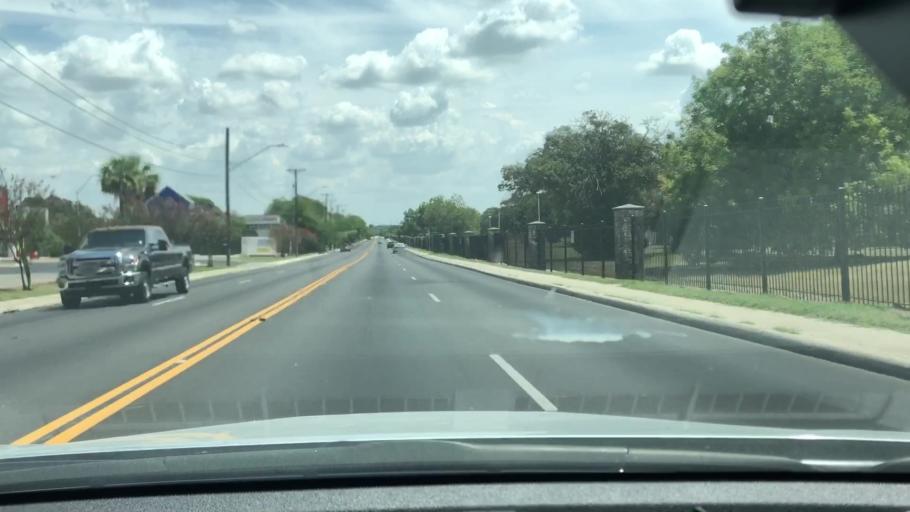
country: US
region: Texas
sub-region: Bexar County
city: Terrell Hills
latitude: 29.4848
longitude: -98.4284
